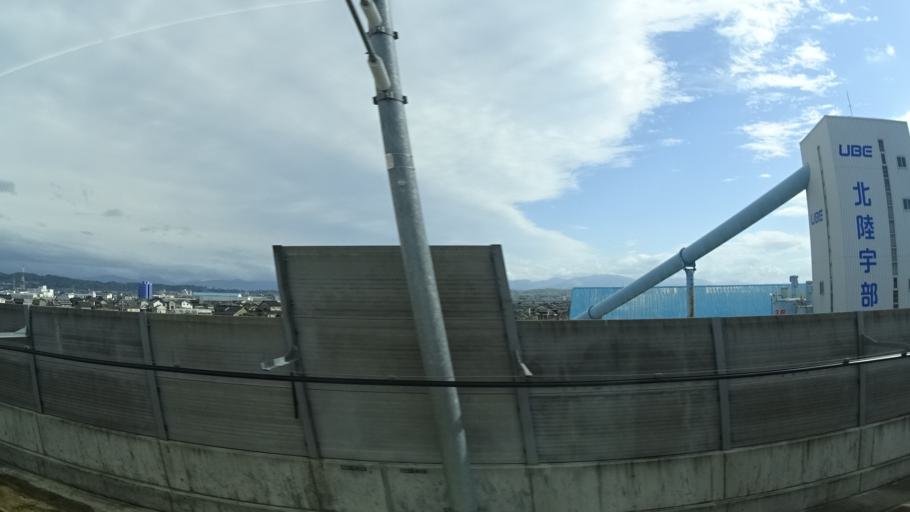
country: JP
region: Toyama
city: Kuragaki-kosugi
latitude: 36.7257
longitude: 137.1235
